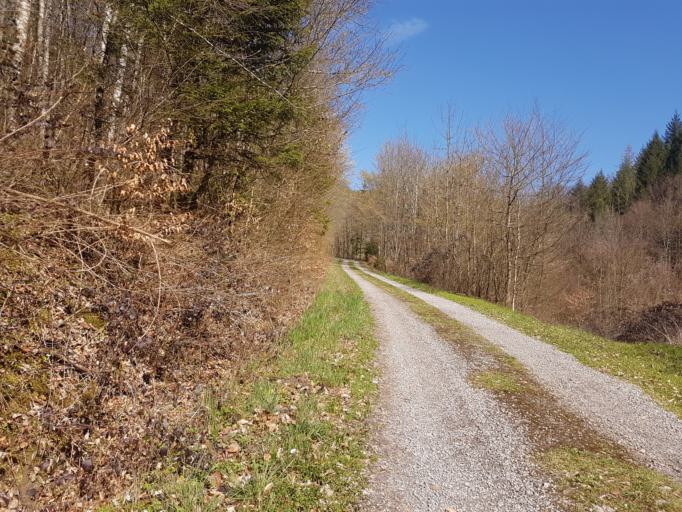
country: DE
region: Baden-Wuerttemberg
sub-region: Regierungsbezirk Stuttgart
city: Jagsthausen
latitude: 49.3386
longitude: 9.4914
